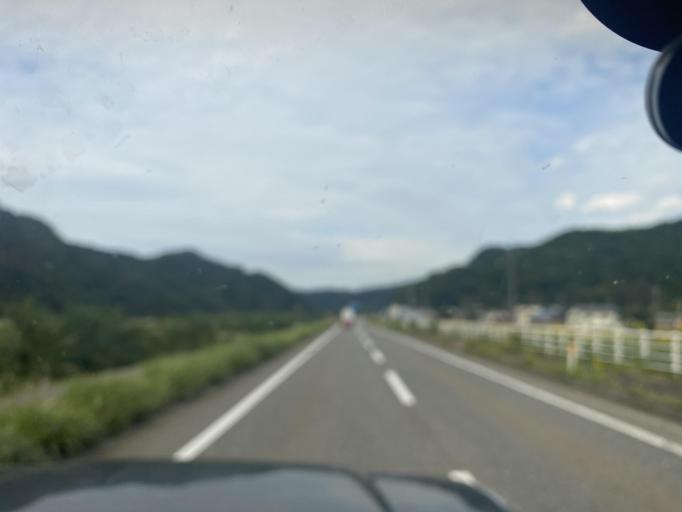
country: JP
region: Niigata
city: Itoigawa
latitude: 36.9659
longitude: 137.8659
